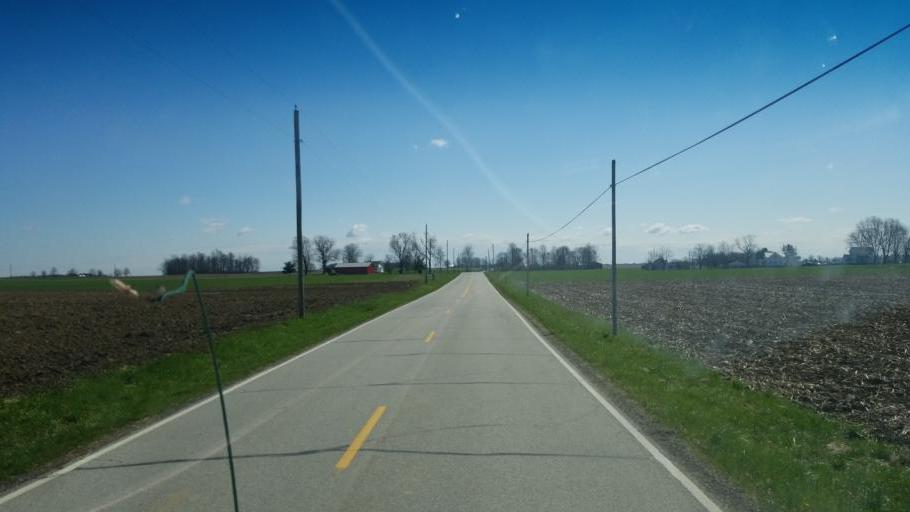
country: US
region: Ohio
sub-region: Crawford County
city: Bucyrus
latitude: 40.8652
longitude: -82.9445
